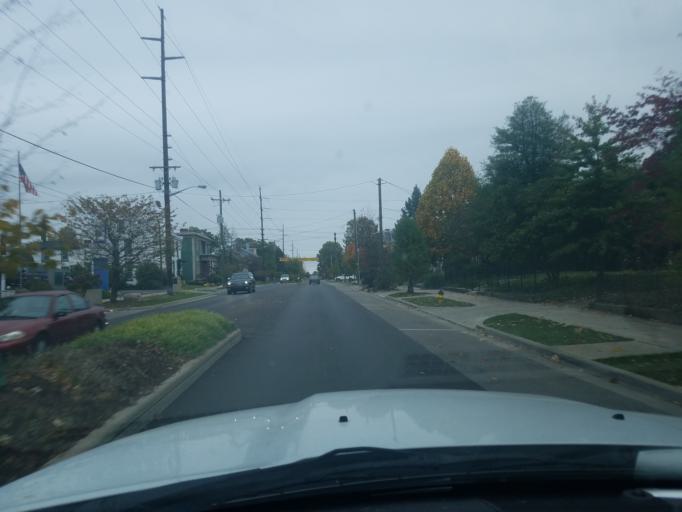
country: US
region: Indiana
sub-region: Floyd County
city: New Albany
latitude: 38.2861
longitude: -85.8149
